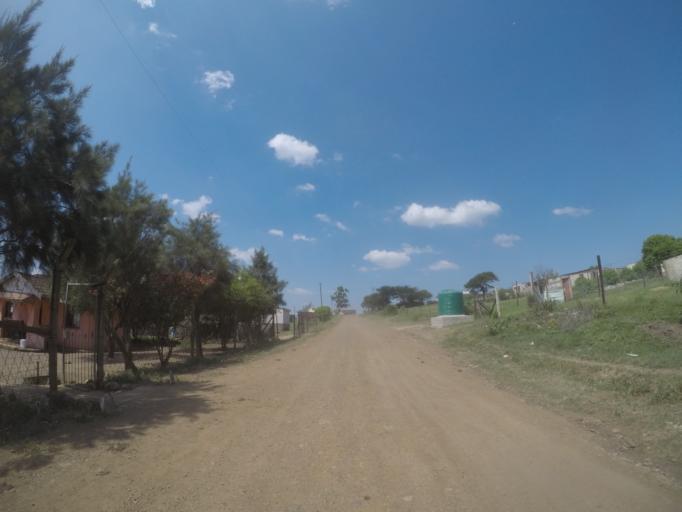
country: ZA
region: KwaZulu-Natal
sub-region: uThungulu District Municipality
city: Empangeni
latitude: -28.5890
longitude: 31.7417
